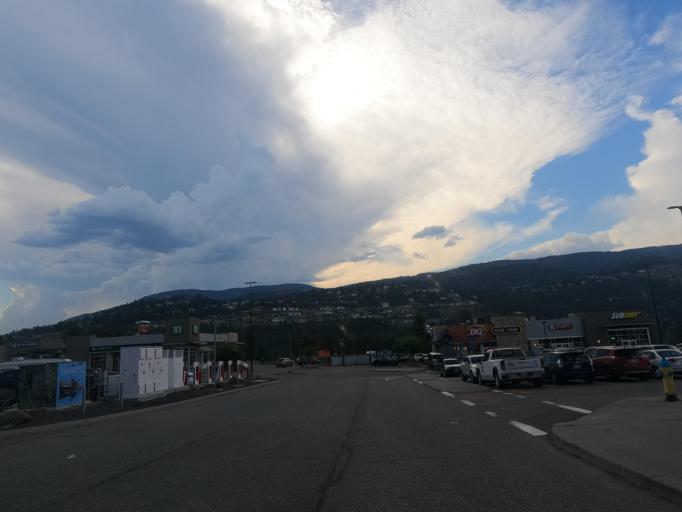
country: CA
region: British Columbia
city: Kelowna
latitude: 49.8800
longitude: -119.5353
